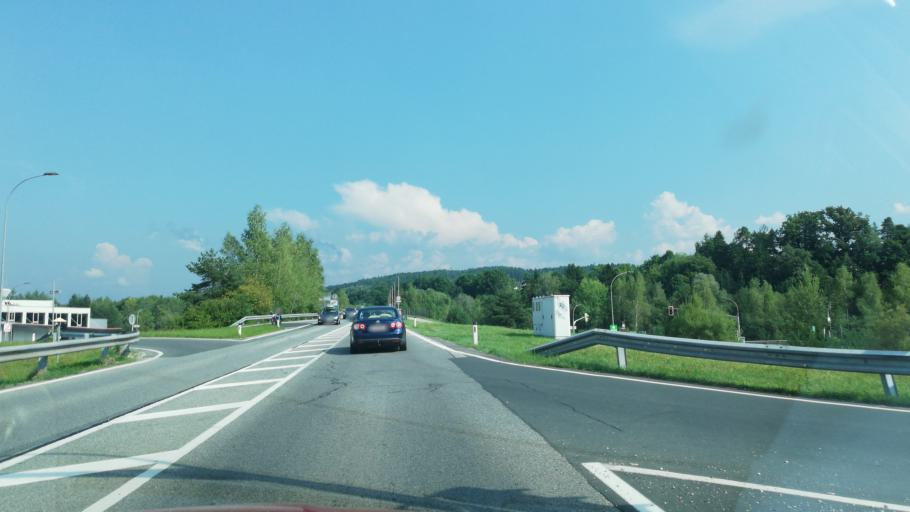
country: AT
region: Carinthia
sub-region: Villach Stadt
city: Villach
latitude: 46.6038
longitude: 13.8724
